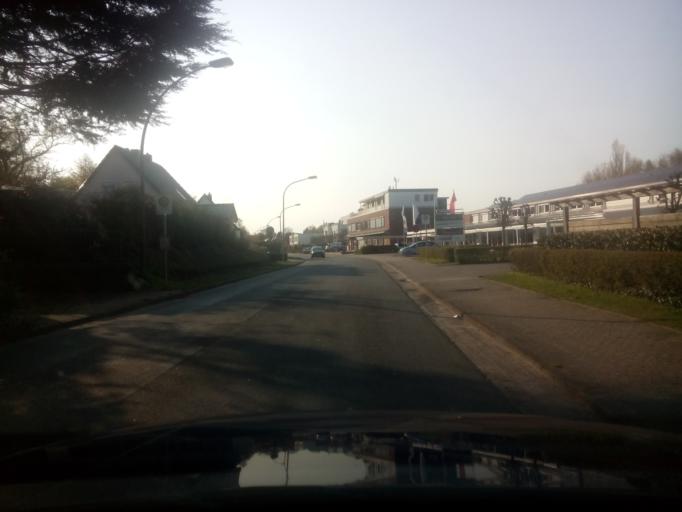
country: DE
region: Lower Saxony
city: Ritterhude
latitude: 53.1858
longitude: 8.7540
